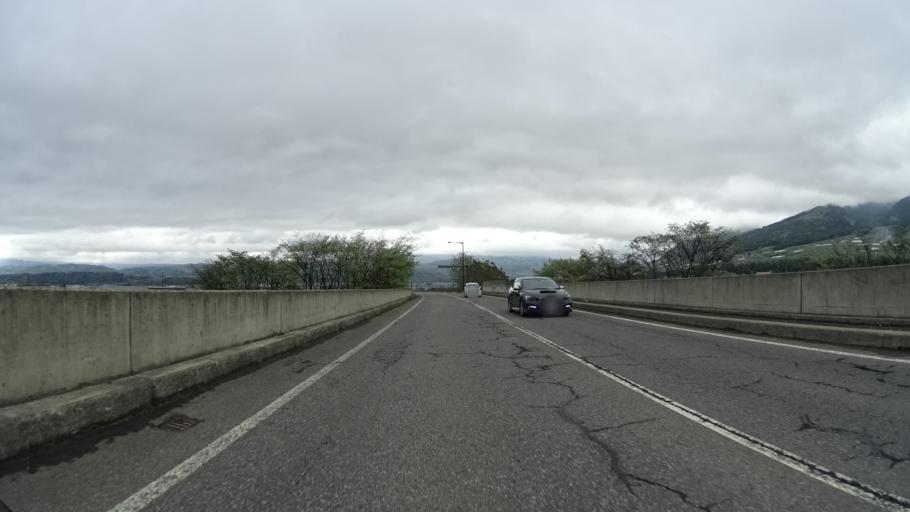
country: JP
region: Nagano
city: Nakano
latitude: 36.7588
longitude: 138.3902
